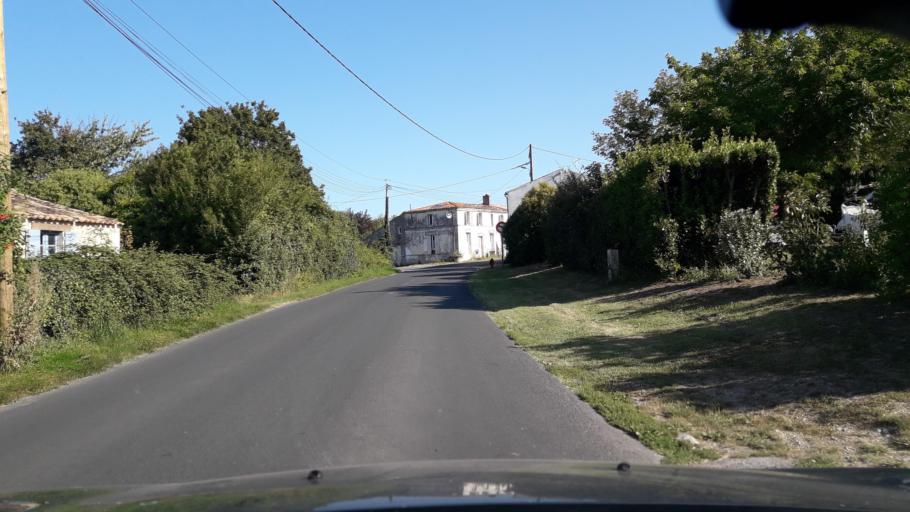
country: FR
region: Poitou-Charentes
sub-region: Departement de la Charente-Maritime
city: Etaules
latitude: 45.7112
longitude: -1.1129
